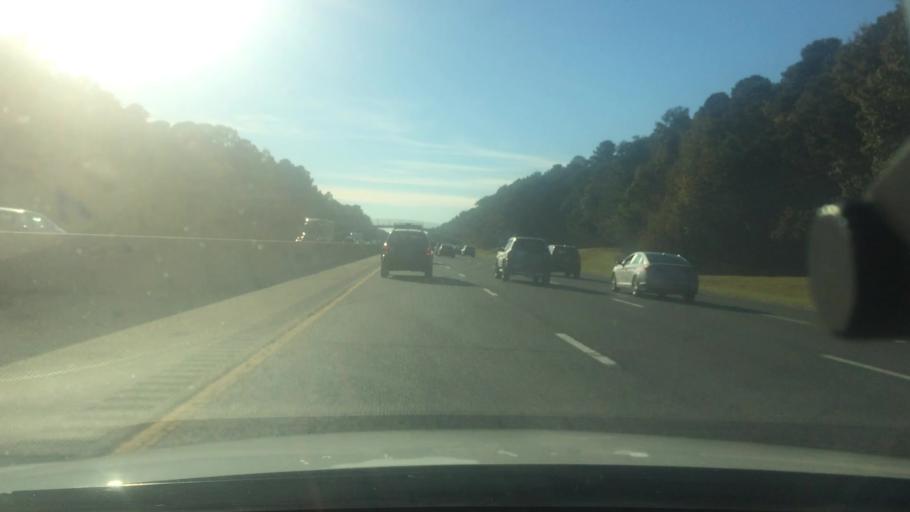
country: US
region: North Carolina
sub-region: Durham County
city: Durham
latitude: 35.9082
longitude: -78.9393
